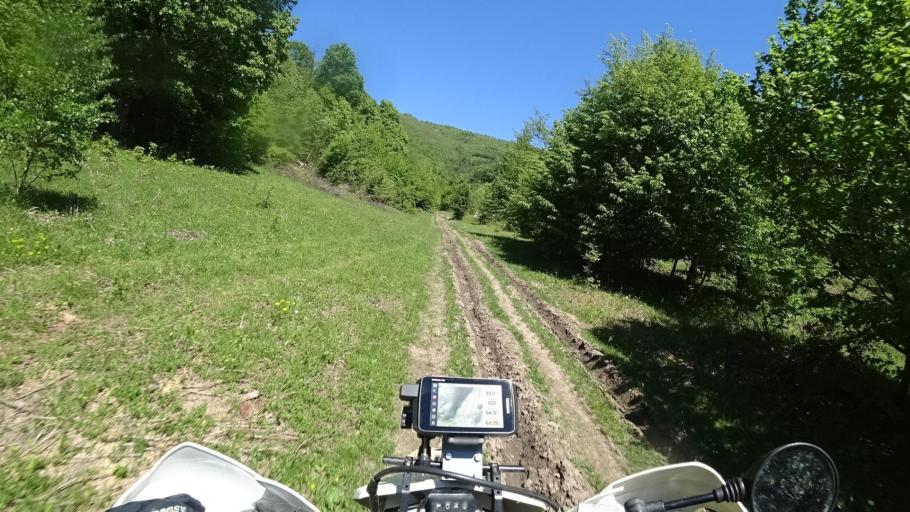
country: BA
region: Republika Srpska
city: Skender Vakuf
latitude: 44.4860
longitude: 17.2349
